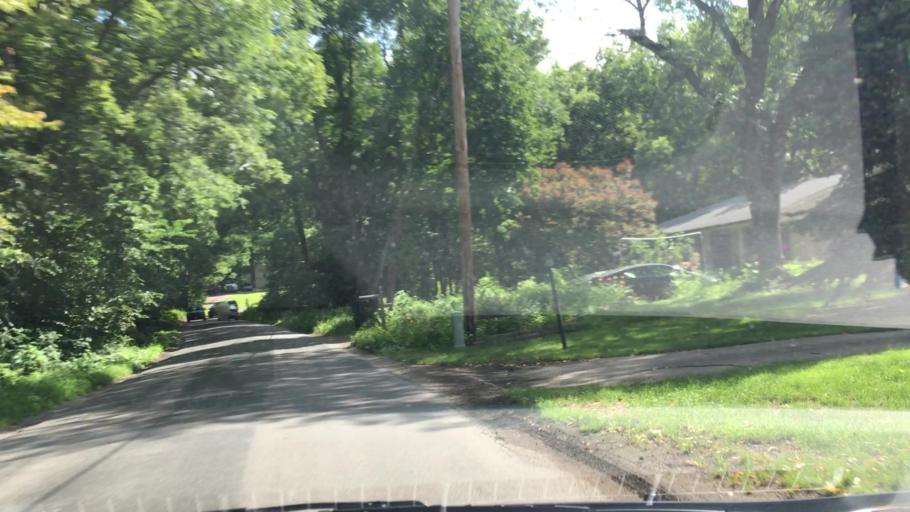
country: US
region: Iowa
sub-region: Johnson County
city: Iowa City
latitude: 41.6900
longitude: -91.5352
